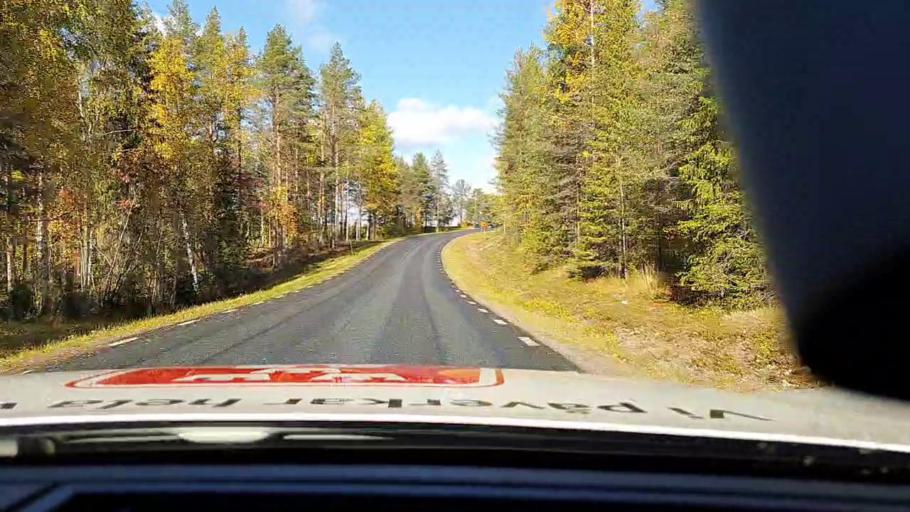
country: SE
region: Vaesterbotten
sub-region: Skelleftea Kommun
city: Langsele
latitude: 65.0025
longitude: 20.0913
